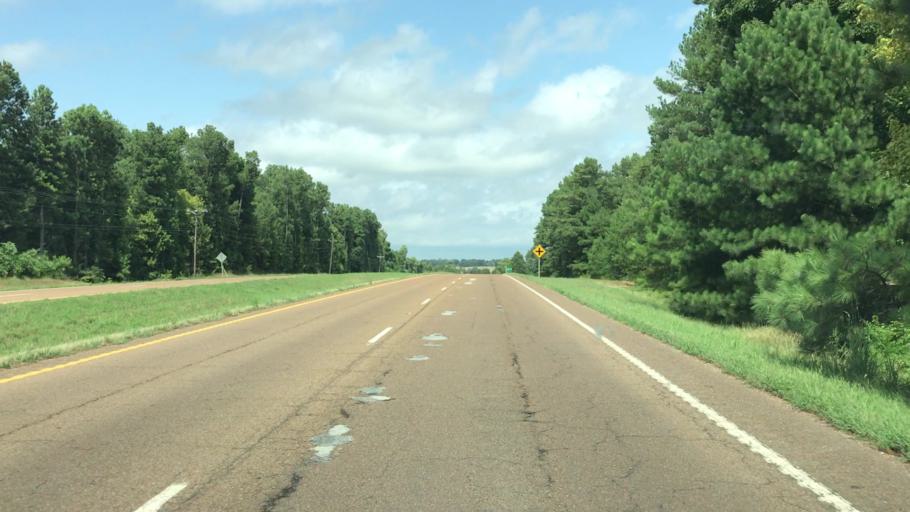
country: US
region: Tennessee
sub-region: Obion County
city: Englewood
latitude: 36.3567
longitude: -89.1372
